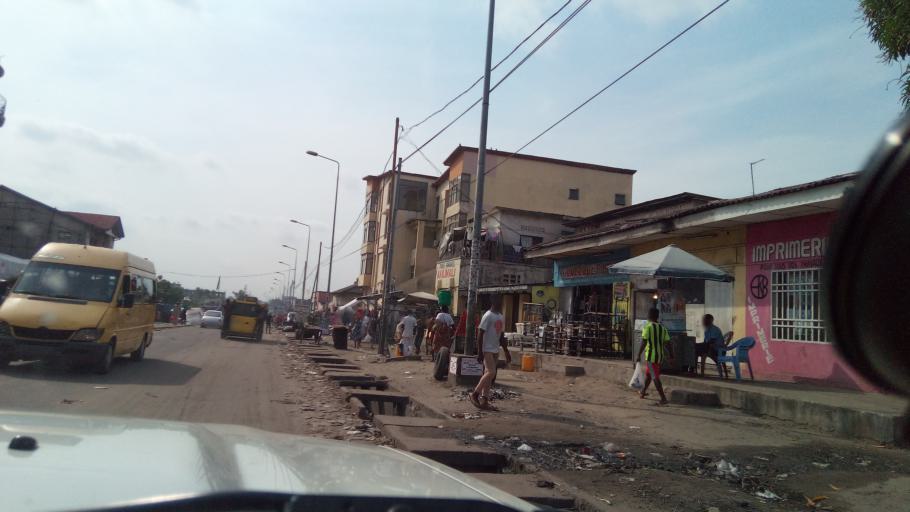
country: CD
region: Kinshasa
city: Kinshasa
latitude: -4.3472
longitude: 15.3130
